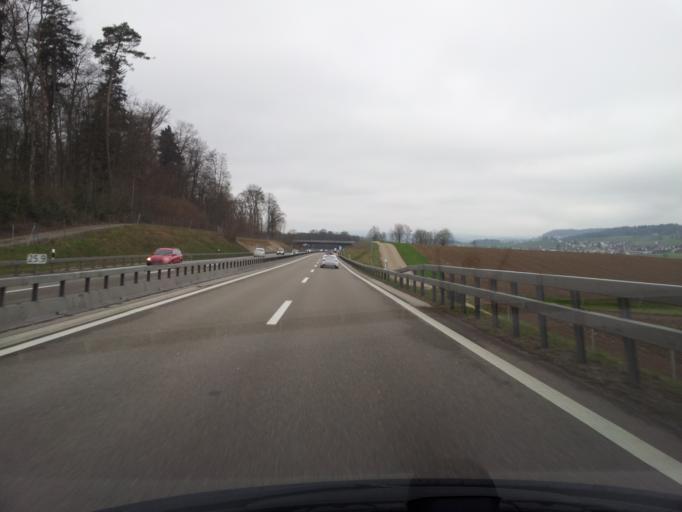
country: CH
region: Zurich
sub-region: Bezirk Andelfingen
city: Marthalen
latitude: 47.6336
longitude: 8.6662
